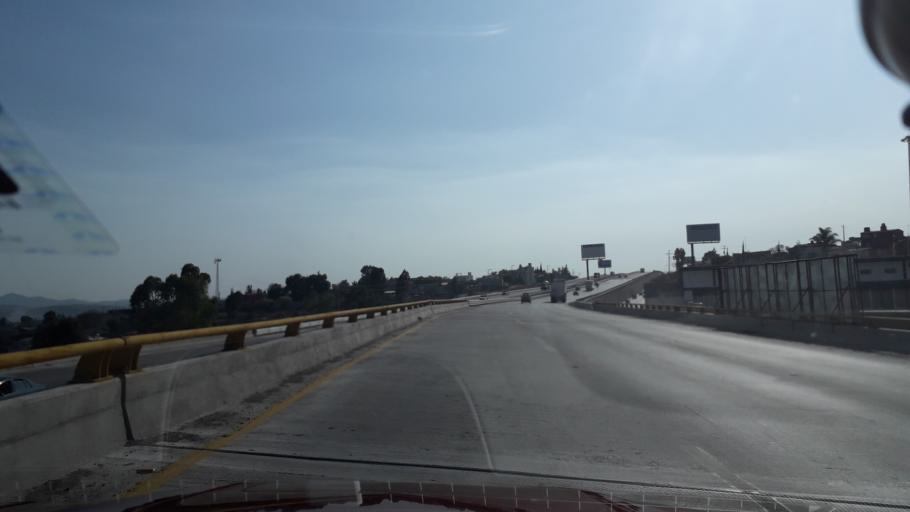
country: MX
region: Puebla
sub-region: Puebla
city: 18 de Marzo
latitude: 18.9728
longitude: -98.1918
